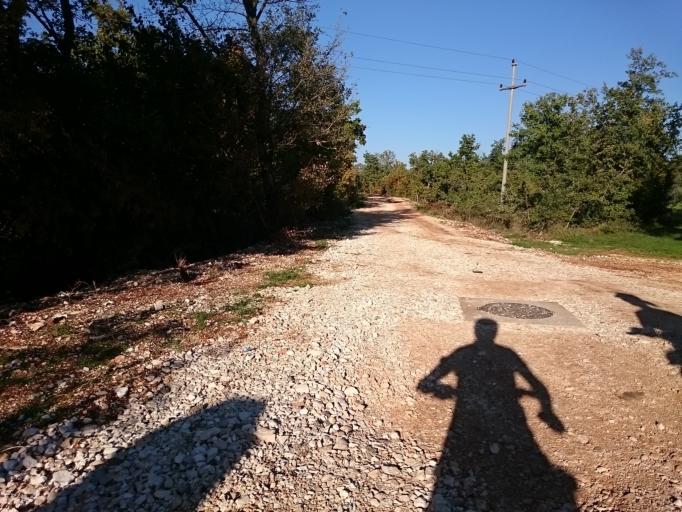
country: HR
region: Istarska
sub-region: Grad Porec
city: Porec
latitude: 45.2611
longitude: 13.6411
